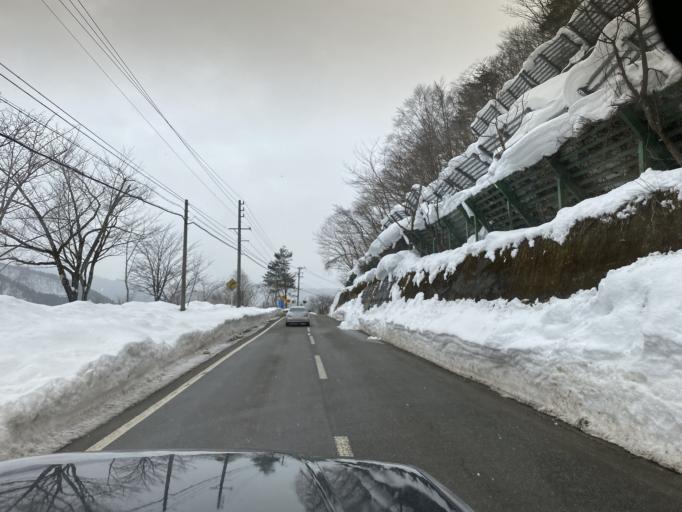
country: JP
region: Gifu
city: Takayama
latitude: 36.0885
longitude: 136.9419
